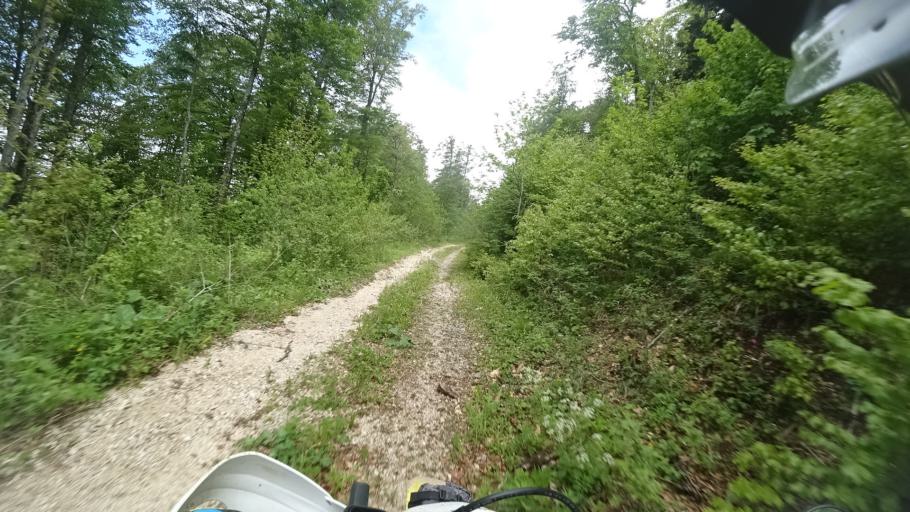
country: BA
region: Federation of Bosnia and Herzegovina
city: Orasac
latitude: 44.5687
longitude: 15.8692
